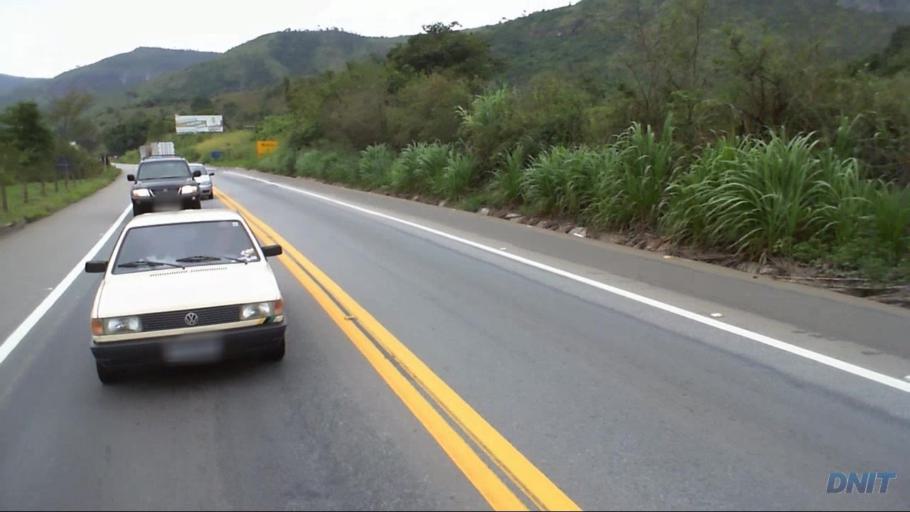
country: BR
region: Minas Gerais
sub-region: Timoteo
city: Timoteo
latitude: -19.5985
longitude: -42.7488
